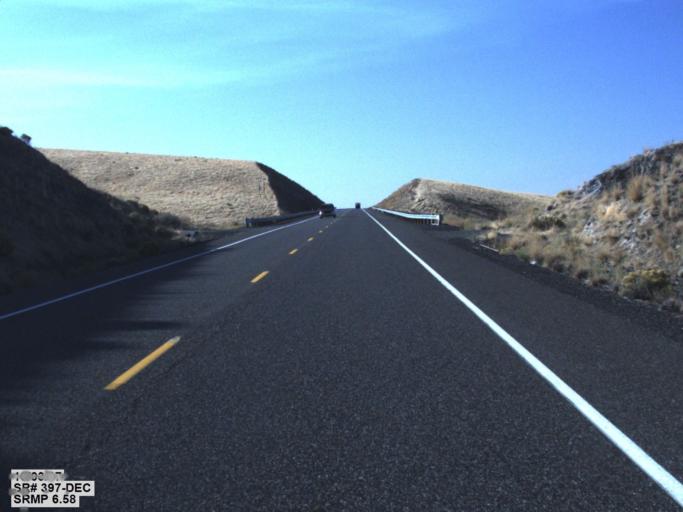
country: US
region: Washington
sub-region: Benton County
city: Highland
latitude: 46.1303
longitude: -119.0793
